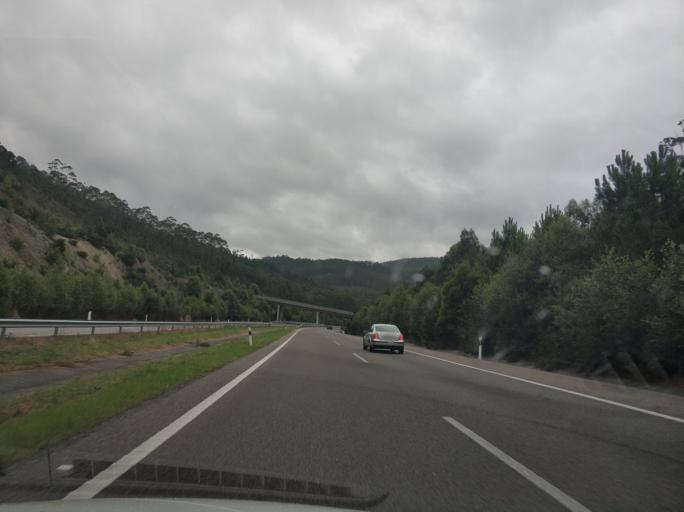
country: ES
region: Galicia
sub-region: Provincia de Lugo
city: Ribadeo
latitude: 43.5344
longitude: -7.0944
